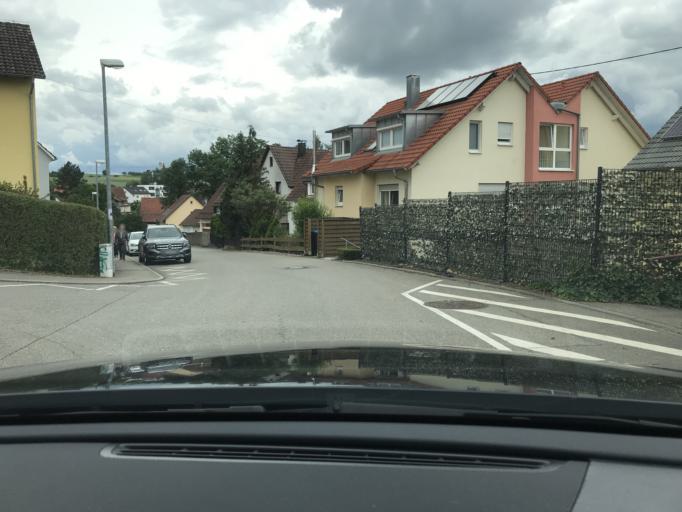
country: DE
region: Baden-Wuerttemberg
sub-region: Regierungsbezirk Stuttgart
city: Affalterbach
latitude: 48.8892
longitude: 9.3152
